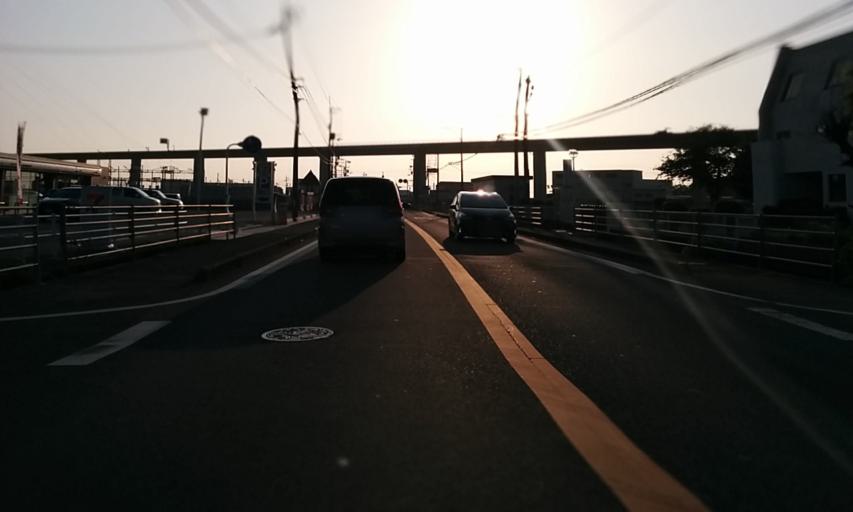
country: JP
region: Ehime
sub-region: Shikoku-chuo Shi
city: Matsuyama
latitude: 33.7896
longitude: 132.7743
